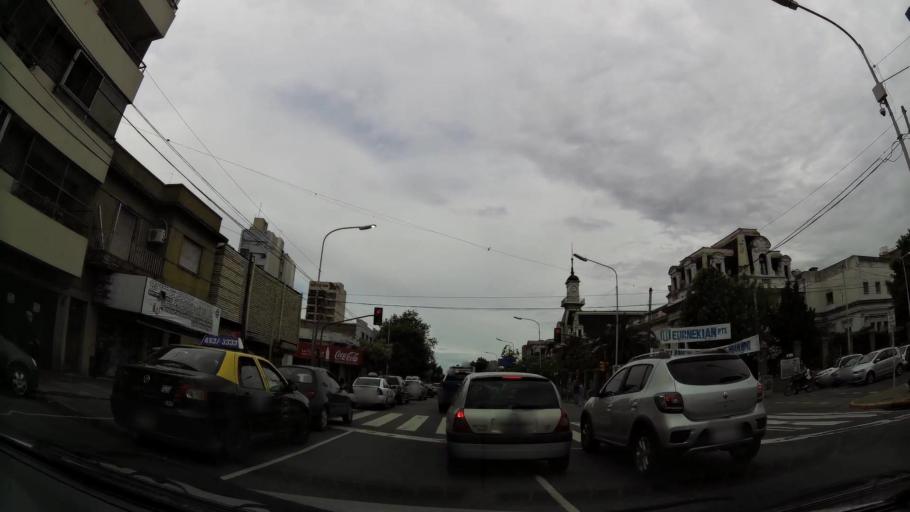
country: AR
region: Buenos Aires
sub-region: Partido de Avellaneda
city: Avellaneda
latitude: -34.6656
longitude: -58.3656
